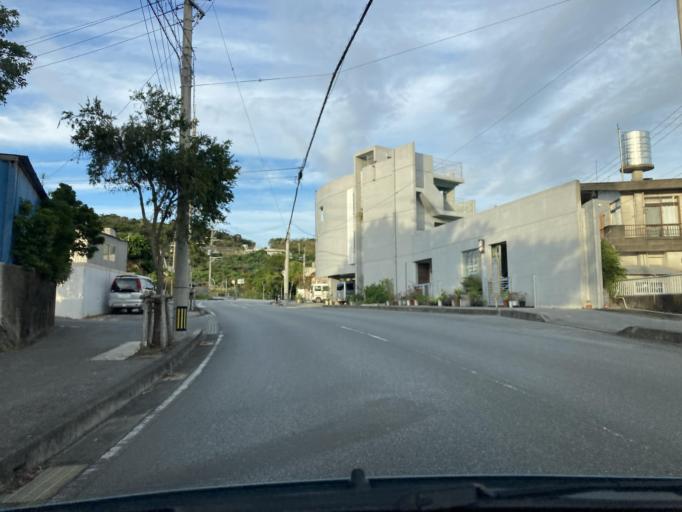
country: JP
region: Okinawa
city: Tomigusuku
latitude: 26.1505
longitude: 127.7024
